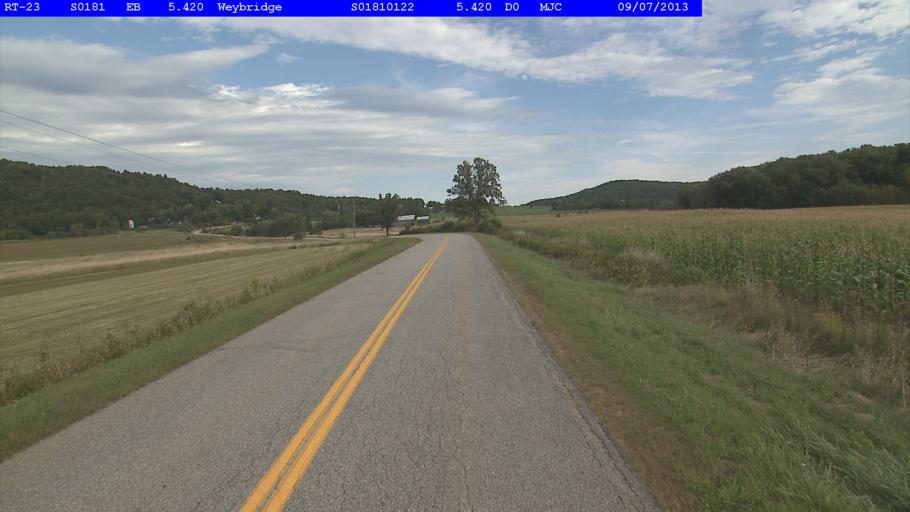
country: US
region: Vermont
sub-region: Addison County
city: Middlebury (village)
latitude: 44.0690
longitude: -73.2503
